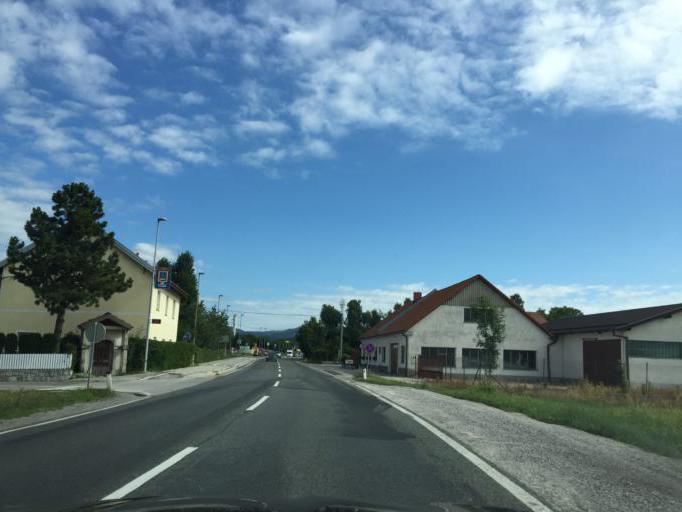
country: SI
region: Postojna
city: Postojna
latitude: 45.7646
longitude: 14.1971
